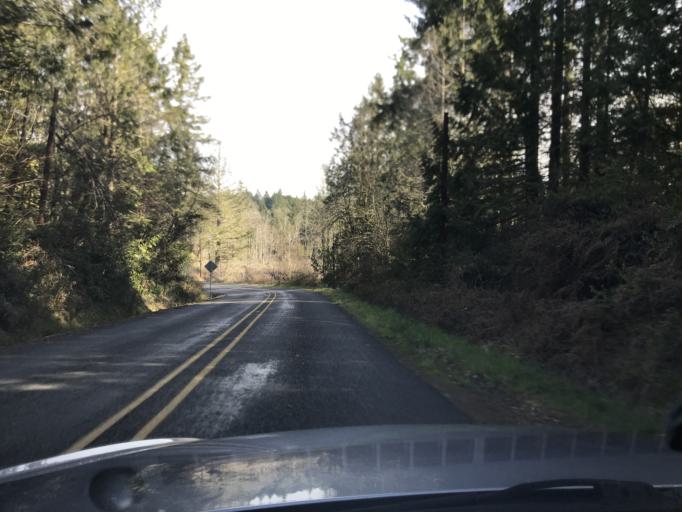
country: US
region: Washington
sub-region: Pierce County
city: Home
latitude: 47.2509
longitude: -122.7570
